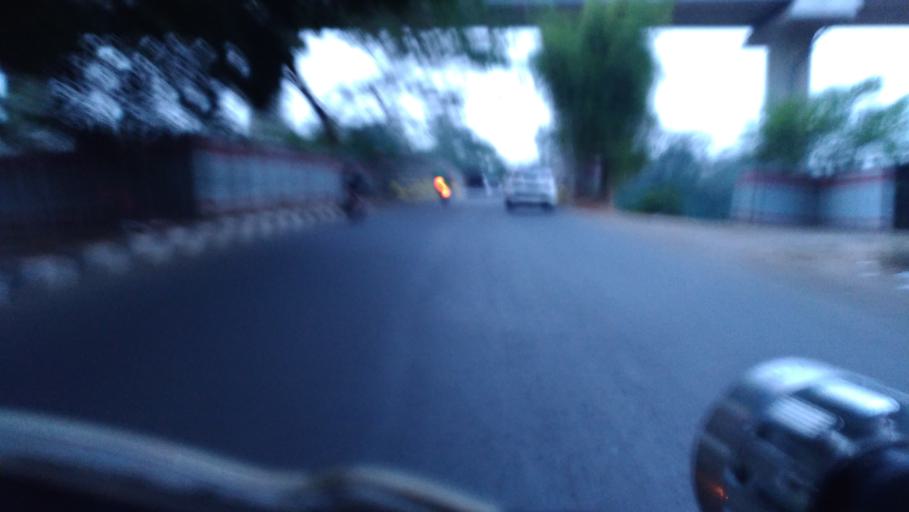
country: ID
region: West Java
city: Cileungsir
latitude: -6.3682
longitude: 106.8943
